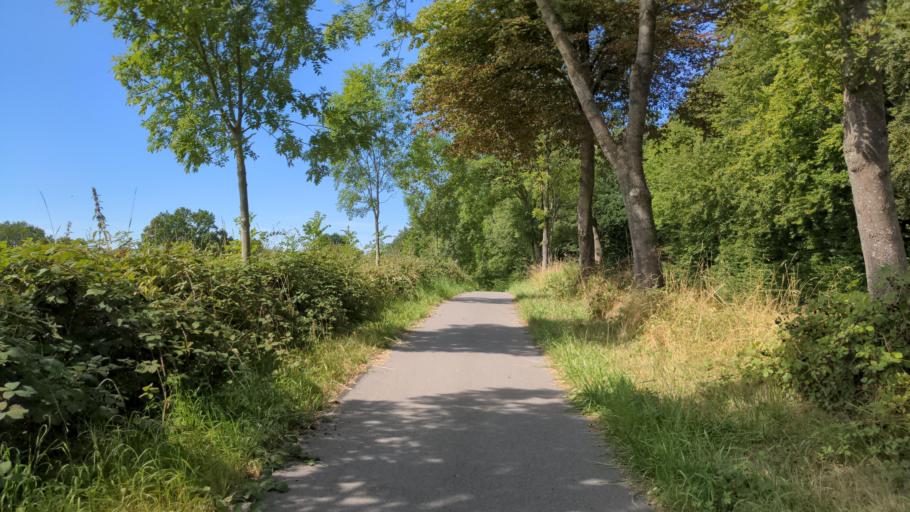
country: DE
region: Schleswig-Holstein
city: Grebin
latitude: 54.1920
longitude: 10.5192
